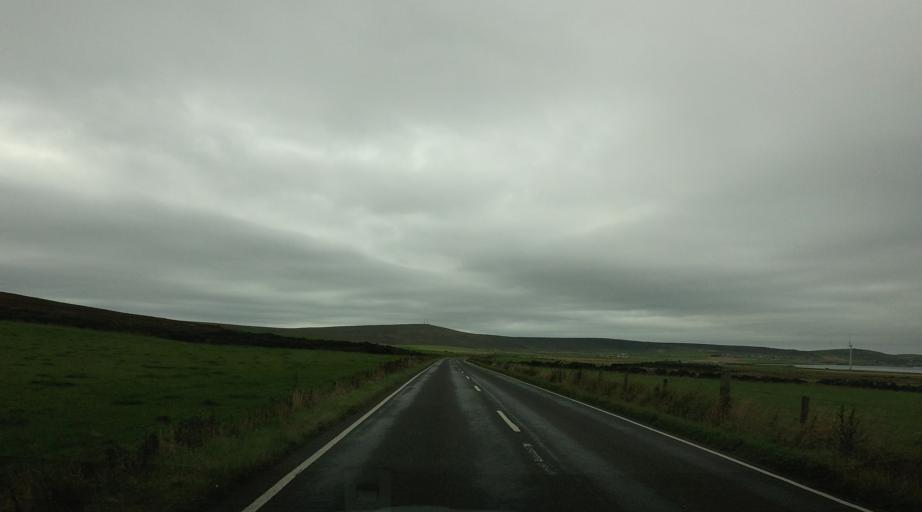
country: GB
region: Scotland
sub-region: Orkney Islands
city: Orkney
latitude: 58.9986
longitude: -3.0310
